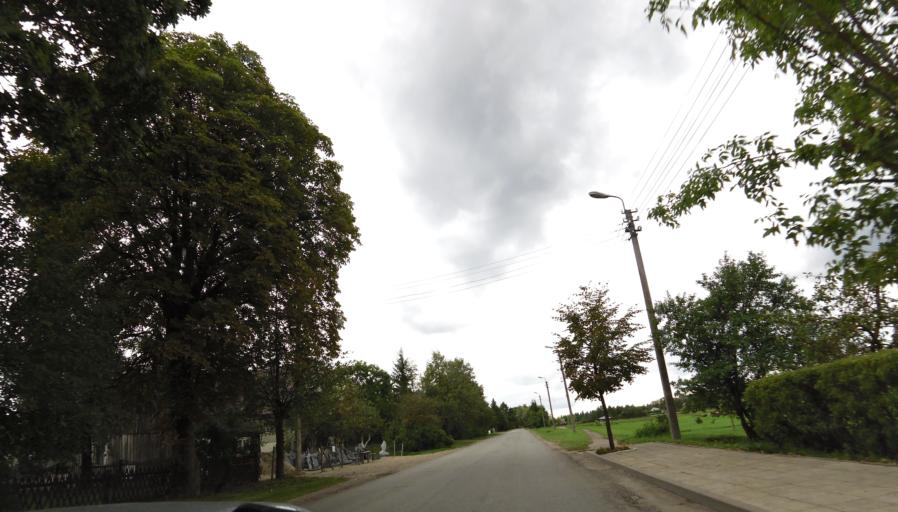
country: LT
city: Linkuva
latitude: 56.0178
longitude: 24.1675
